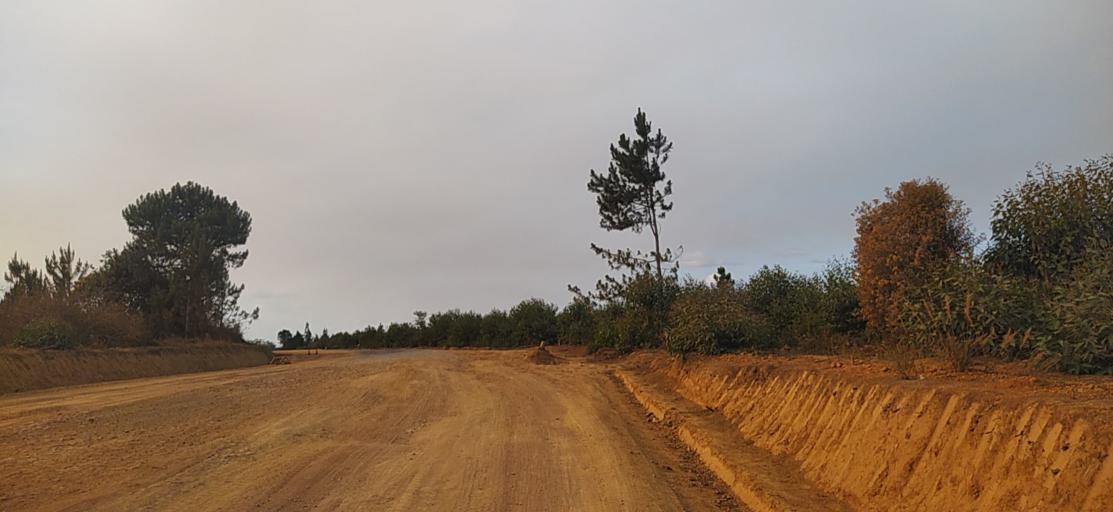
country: MG
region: Alaotra Mangoro
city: Moramanga
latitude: -18.6004
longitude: 48.2787
